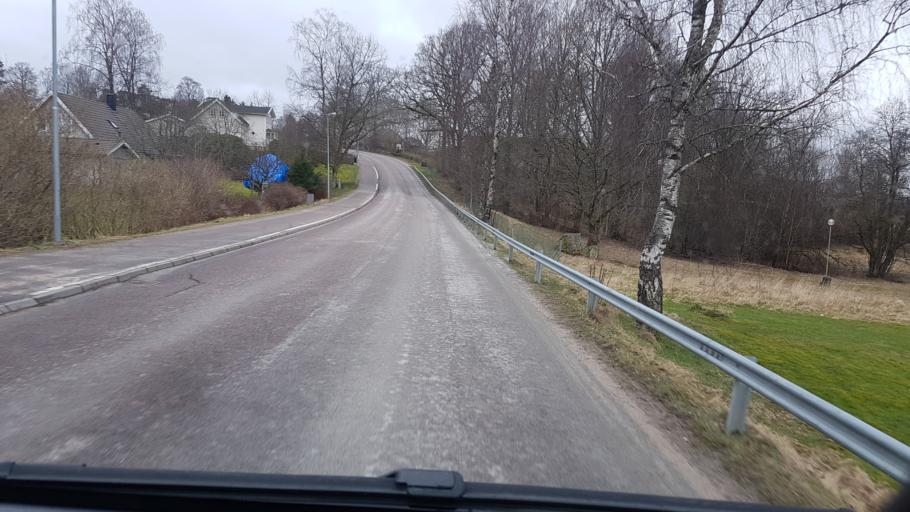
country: SE
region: Vaestra Goetaland
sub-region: Lerums Kommun
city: Stenkullen
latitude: 57.8024
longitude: 12.3785
